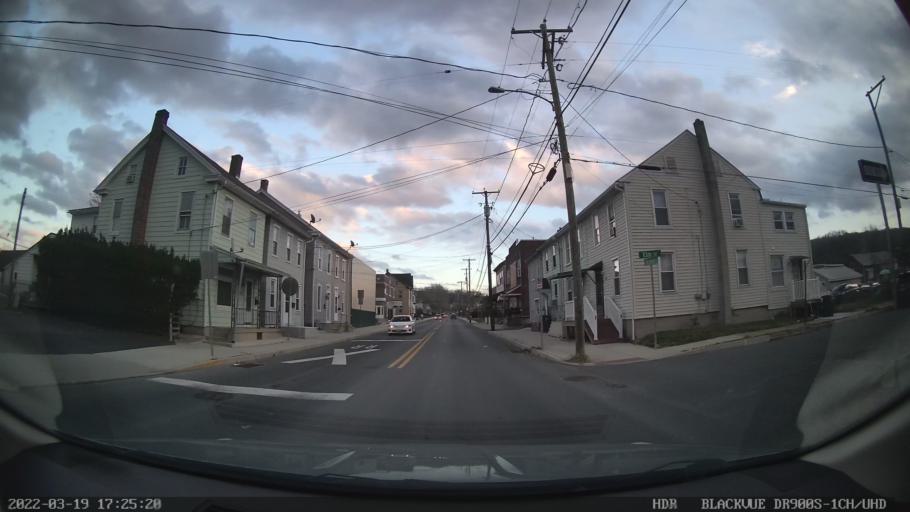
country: US
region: Pennsylvania
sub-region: Berks County
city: Fleetwood
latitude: 40.4517
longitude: -75.8190
